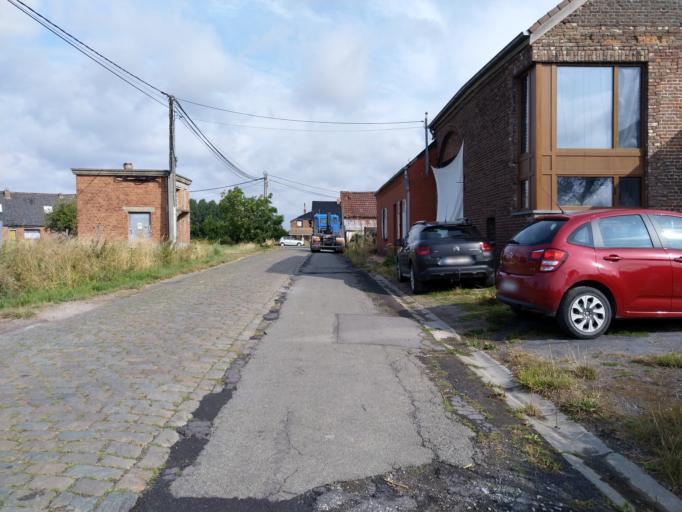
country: BE
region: Wallonia
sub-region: Province du Hainaut
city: Chievres
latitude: 50.5640
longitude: 3.8227
